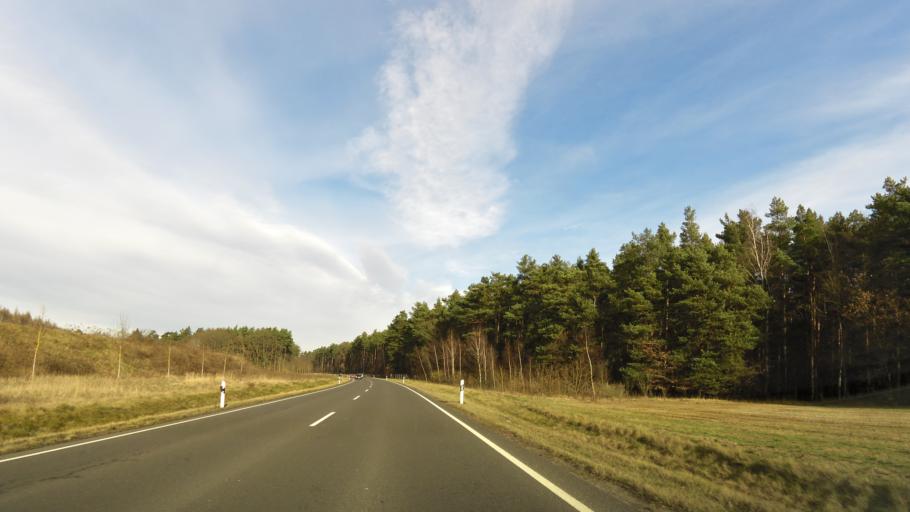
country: DE
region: Brandenburg
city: Michendorf
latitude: 52.3179
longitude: 13.0473
